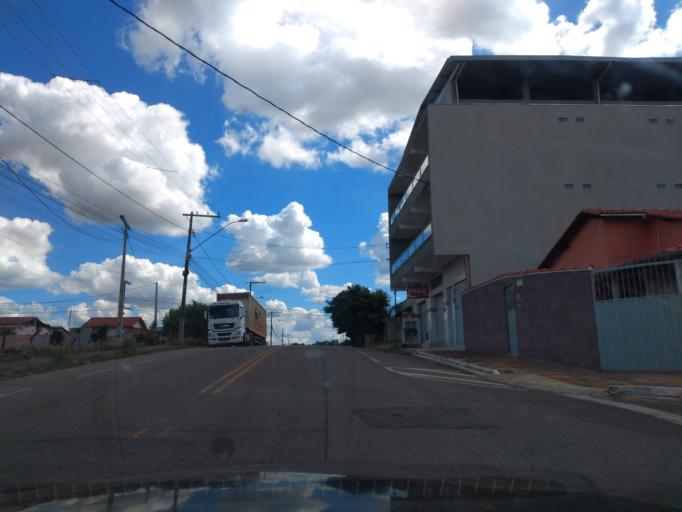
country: BR
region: Minas Gerais
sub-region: Tres Coracoes
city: Tres Coracoes
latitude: -21.6828
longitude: -45.2685
